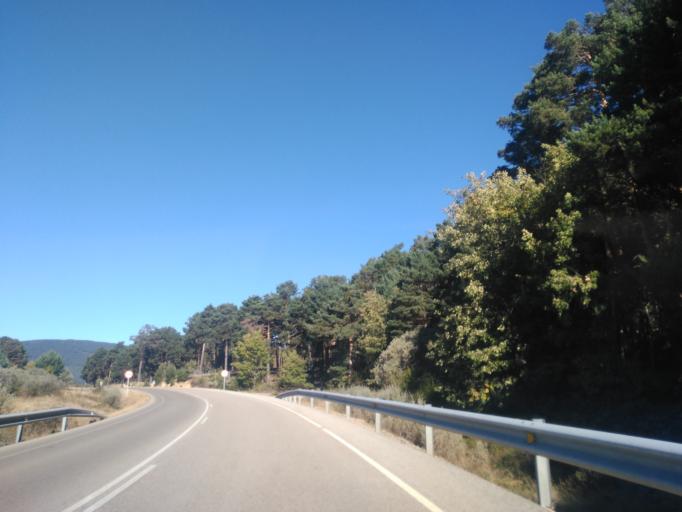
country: ES
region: Castille and Leon
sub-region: Provincia de Soria
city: Vinuesa
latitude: 41.8999
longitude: -2.7364
